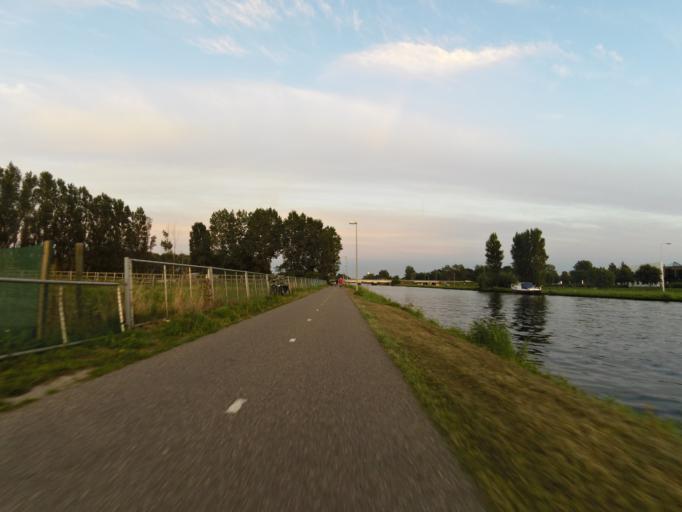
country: NL
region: South Holland
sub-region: Gemeente Oegstgeest
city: Oegstgeest
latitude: 52.1942
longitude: 4.4603
